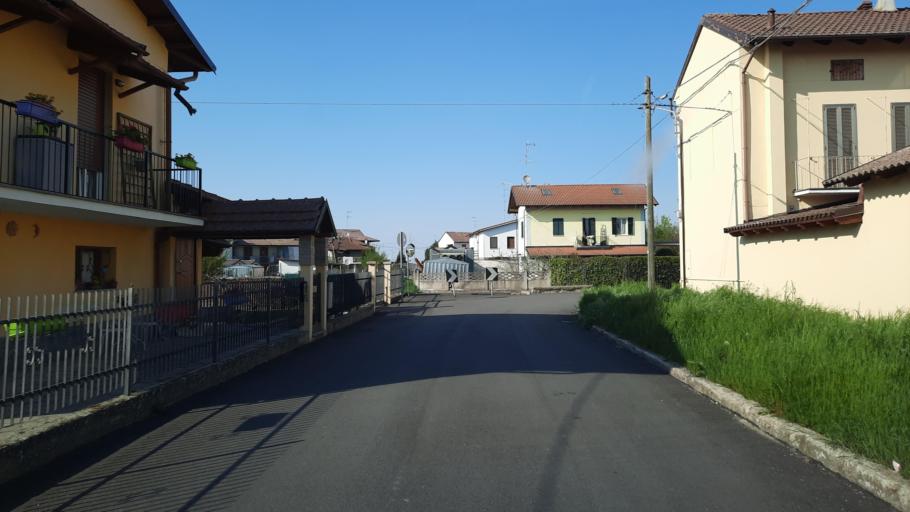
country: IT
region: Piedmont
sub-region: Provincia di Vercelli
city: Lignana
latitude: 45.2852
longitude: 8.3418
